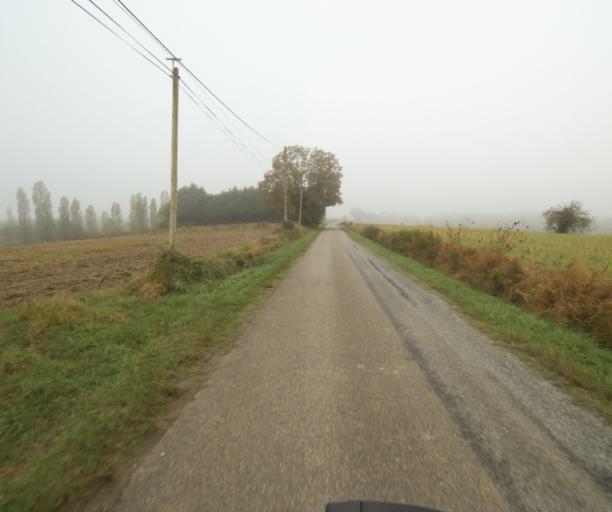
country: FR
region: Midi-Pyrenees
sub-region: Departement du Tarn-et-Garonne
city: Nohic
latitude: 43.9314
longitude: 1.4630
